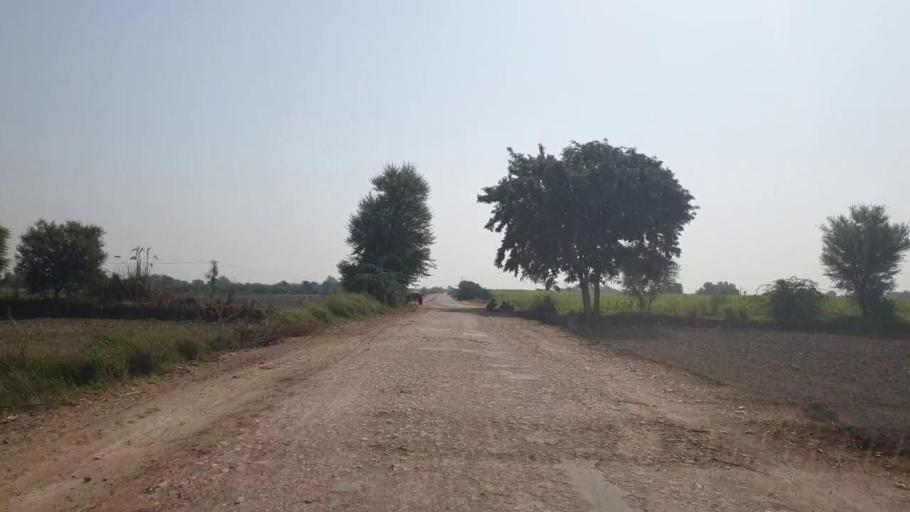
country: PK
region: Sindh
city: Berani
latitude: 25.8853
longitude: 68.7636
